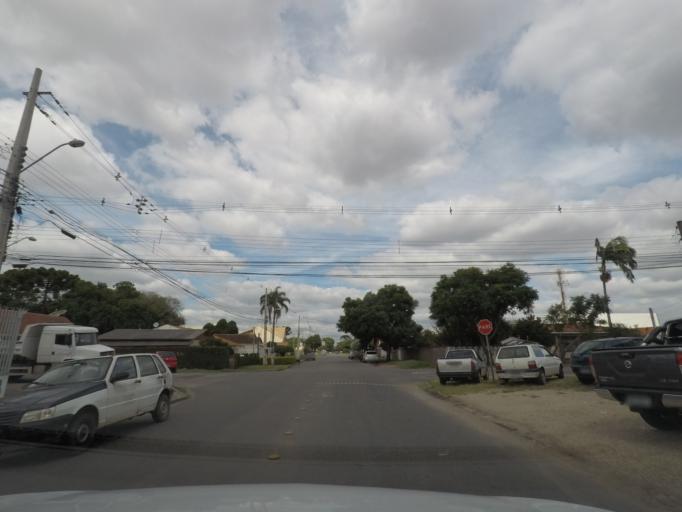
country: BR
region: Parana
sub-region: Sao Jose Dos Pinhais
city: Sao Jose dos Pinhais
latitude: -25.4836
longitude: -49.2437
